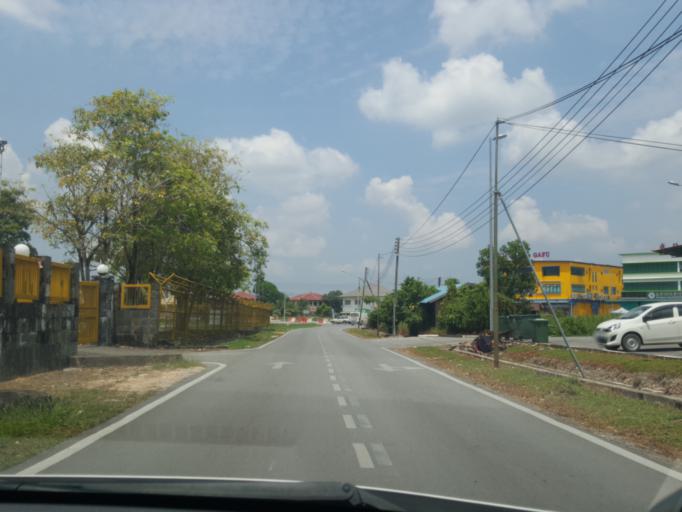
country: MY
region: Sarawak
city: Sarikei
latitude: 2.1285
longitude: 111.5247
